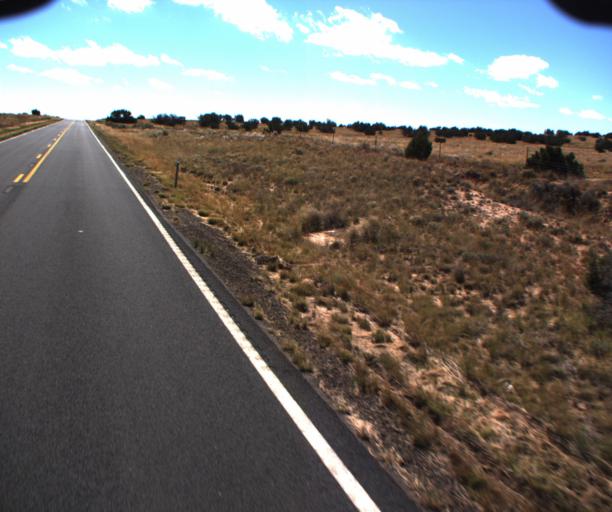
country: US
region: Arizona
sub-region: Apache County
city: Houck
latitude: 35.0135
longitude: -109.2356
